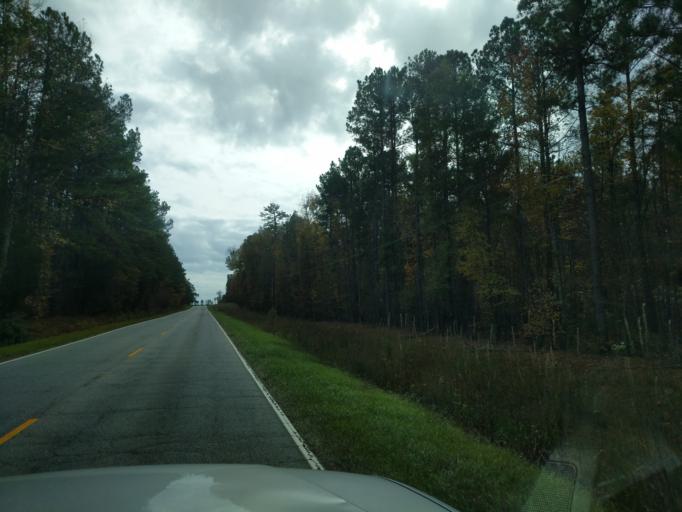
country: US
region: South Carolina
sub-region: Saluda County
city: Saluda
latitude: 34.1184
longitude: -81.8353
